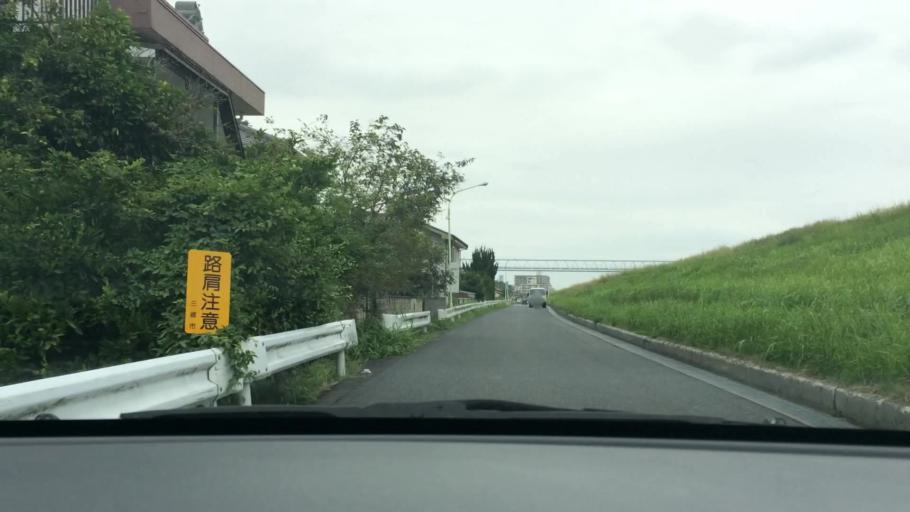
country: JP
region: Chiba
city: Nagareyama
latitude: 35.8348
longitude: 139.8861
